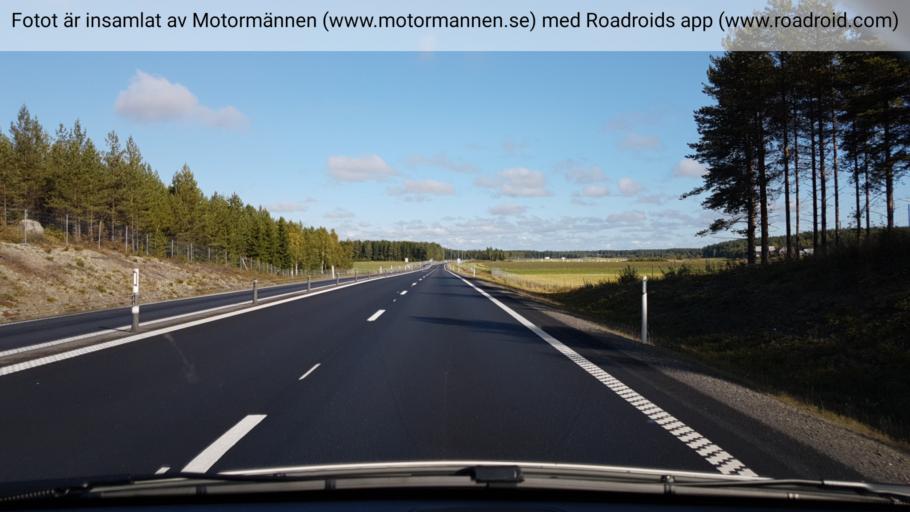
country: SE
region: Vaesterbotten
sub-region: Robertsfors Kommun
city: Robertsfors
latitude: 64.0945
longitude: 20.8693
